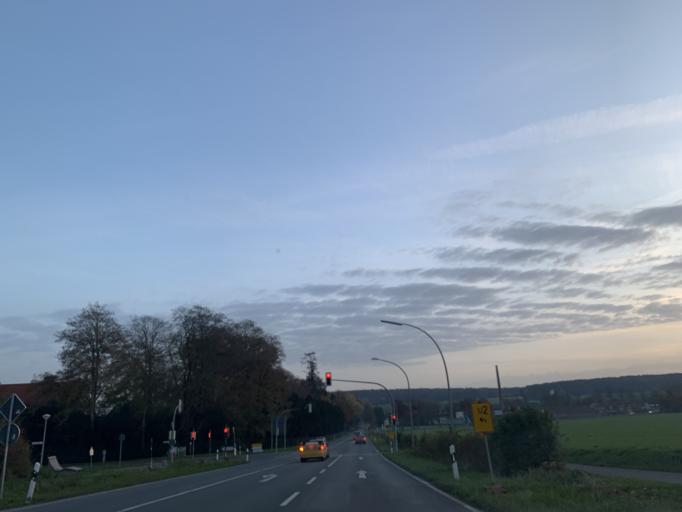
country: DE
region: North Rhine-Westphalia
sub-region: Regierungsbezirk Munster
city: Havixbeck
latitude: 51.9731
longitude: 7.4080
